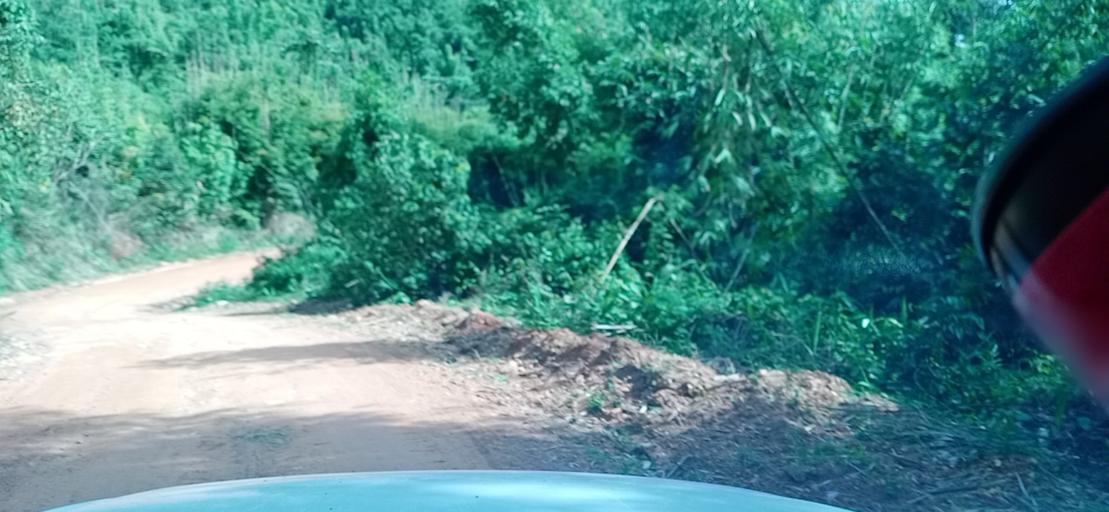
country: TH
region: Changwat Bueng Kan
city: Pak Khat
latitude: 18.6363
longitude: 103.2506
